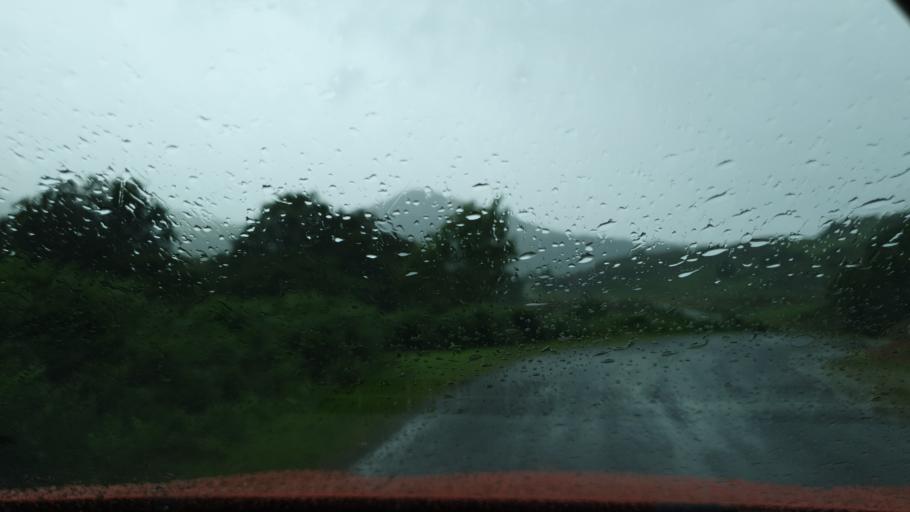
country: GB
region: England
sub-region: Cumbria
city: Millom
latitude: 54.3140
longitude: -3.2302
